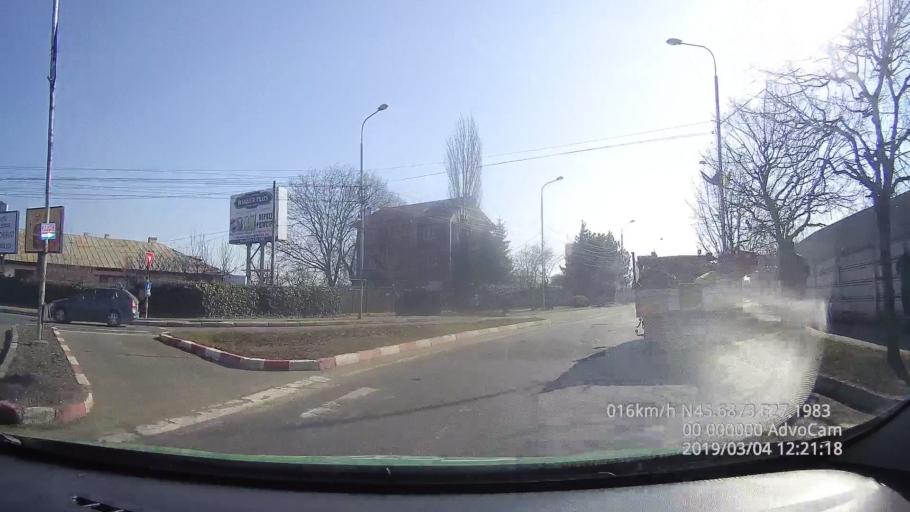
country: RO
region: Vrancea
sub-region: Comuna Vrancioaia
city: Focsani
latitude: 45.6809
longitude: 27.2088
